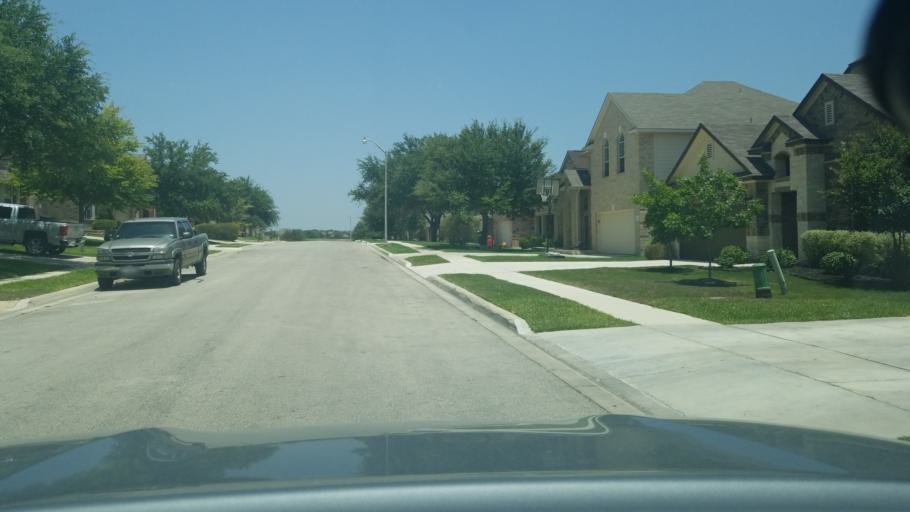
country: US
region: Texas
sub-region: Guadalupe County
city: Cibolo
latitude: 29.5789
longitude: -98.2288
